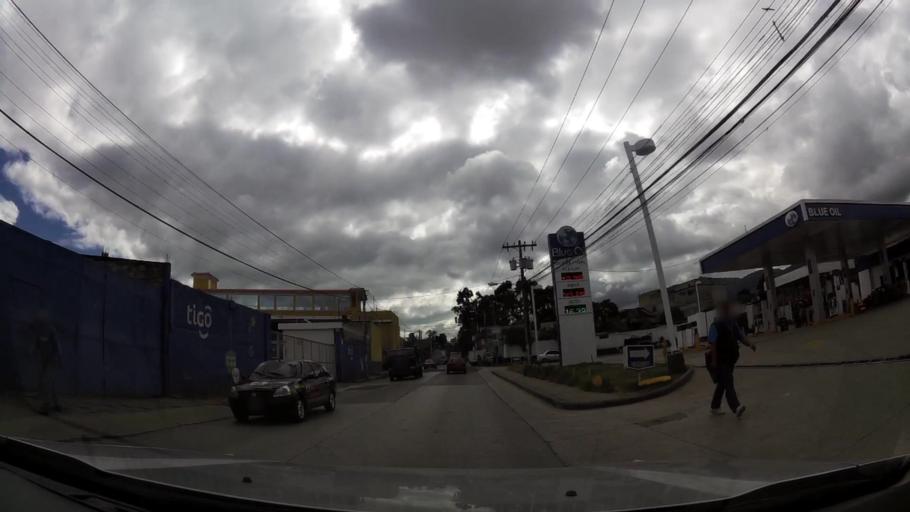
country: GT
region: Guatemala
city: Mixco
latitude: 14.6411
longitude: -90.5965
